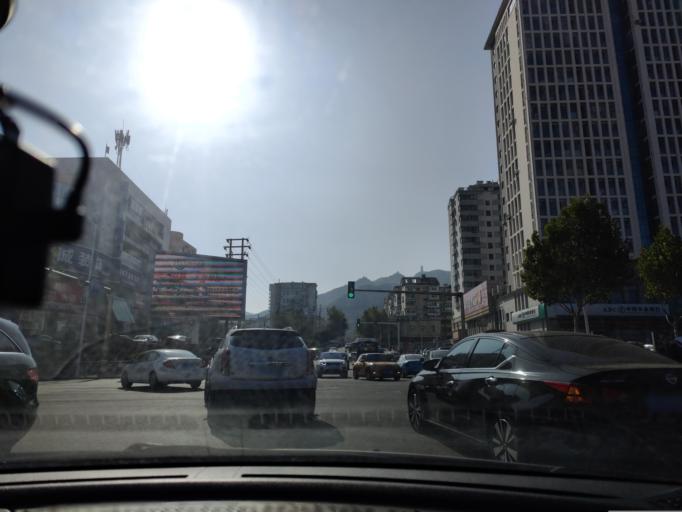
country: CN
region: Shandong Sheng
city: Xiangyang
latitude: 37.5198
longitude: 121.3930
